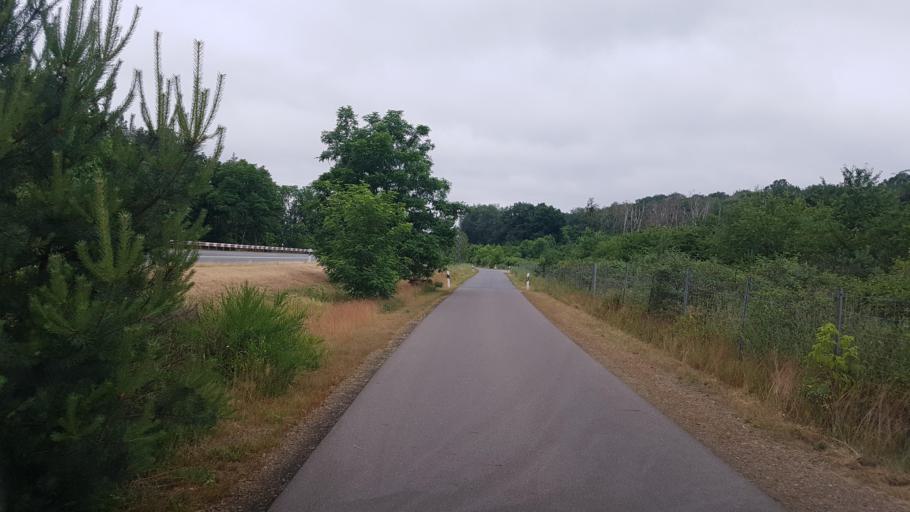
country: DE
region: Brandenburg
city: Schwarzbach
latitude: 51.4890
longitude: 13.9376
